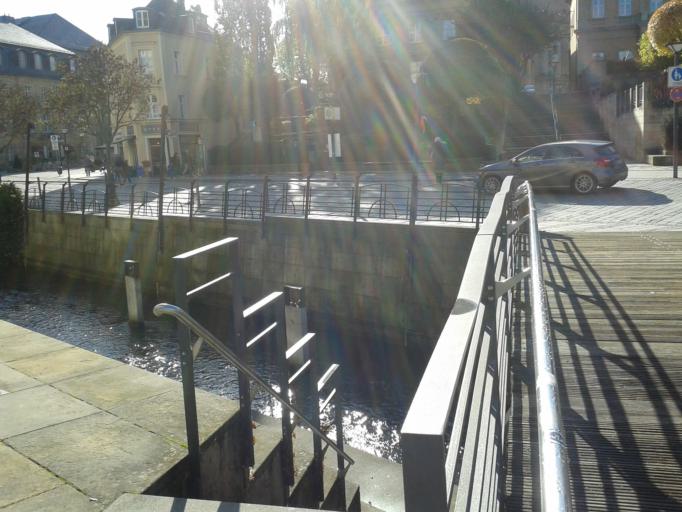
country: DE
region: Bavaria
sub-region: Upper Franconia
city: Bayreuth
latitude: 49.9453
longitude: 11.5772
